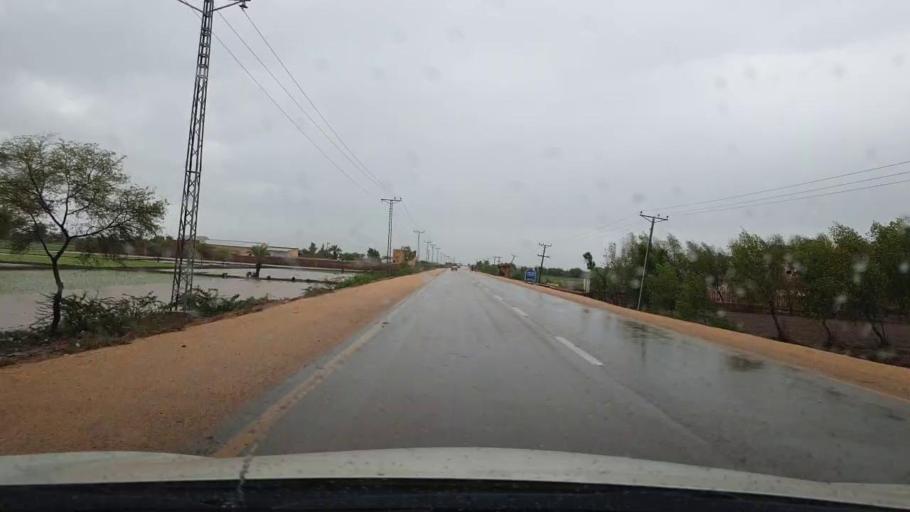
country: PK
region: Sindh
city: Kario
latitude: 24.6536
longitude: 68.5445
